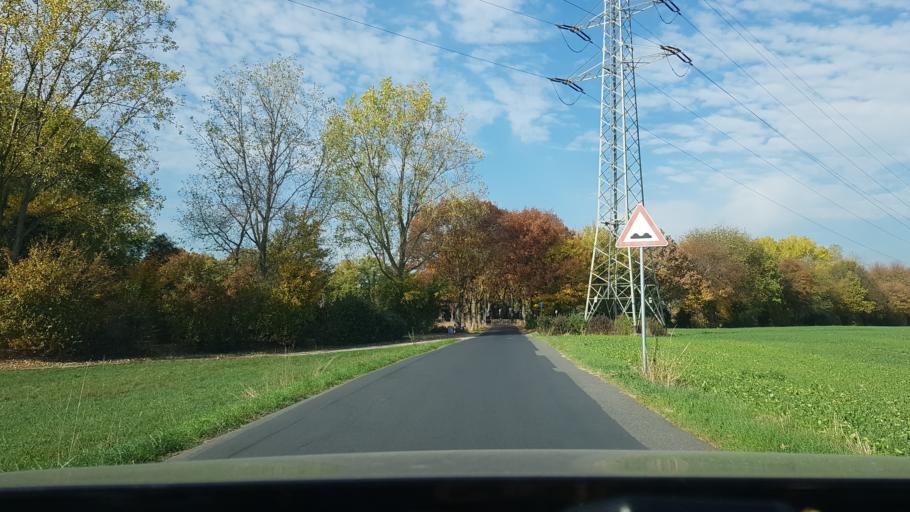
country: DE
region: North Rhine-Westphalia
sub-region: Regierungsbezirk Dusseldorf
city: Moers
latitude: 51.4272
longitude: 6.6195
